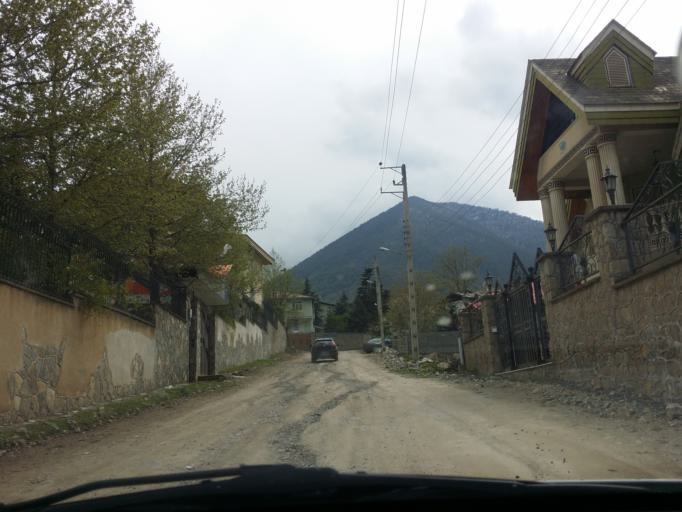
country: IR
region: Mazandaran
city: `Abbasabad
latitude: 36.4865
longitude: 51.1402
